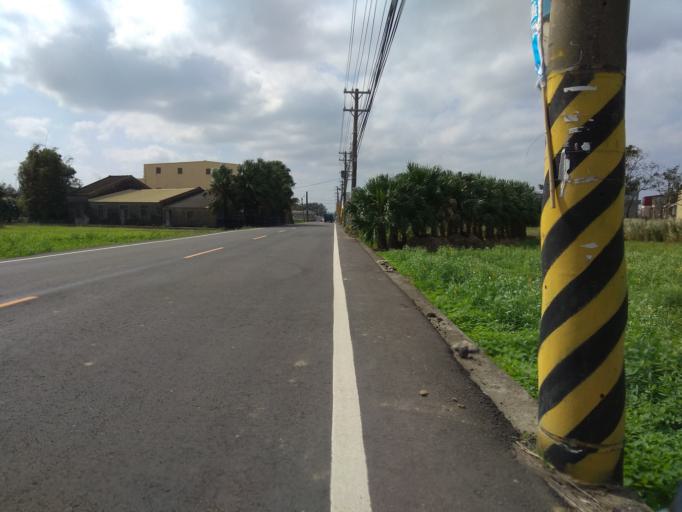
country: TW
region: Taiwan
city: Taoyuan City
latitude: 25.0723
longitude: 121.2485
